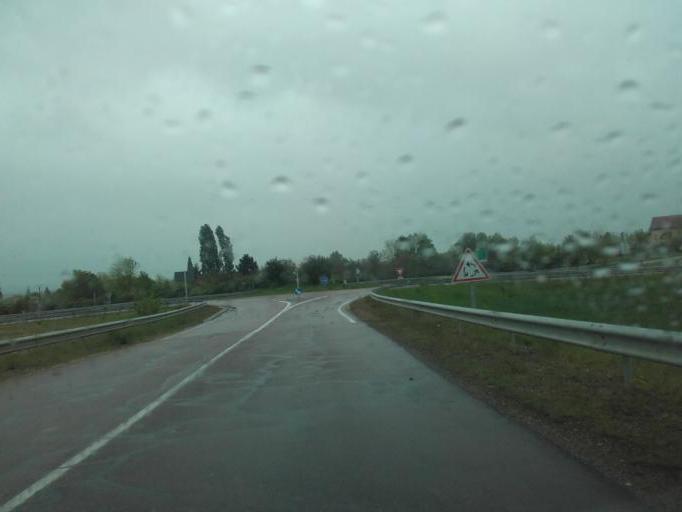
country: FR
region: Bourgogne
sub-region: Departement de Saone-et-Loire
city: Givry
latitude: 46.7569
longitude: 4.7218
